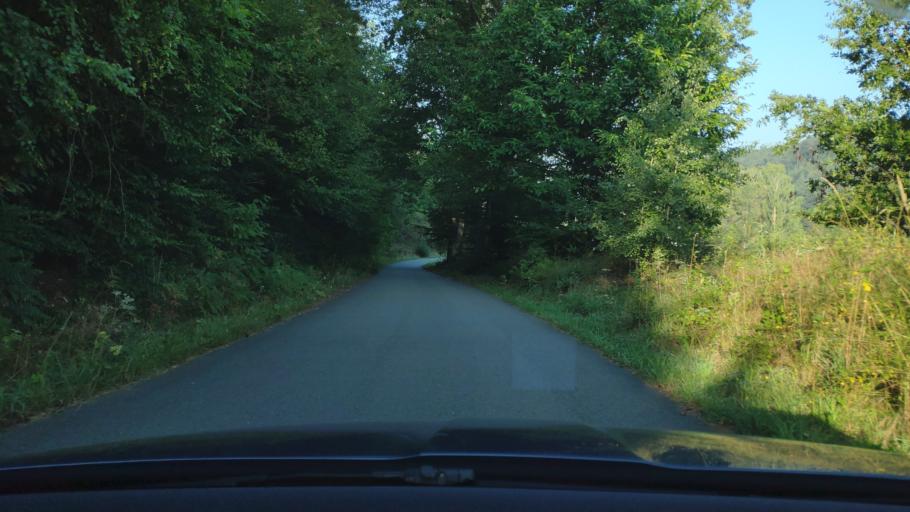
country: DE
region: Rheinland-Pfalz
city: Fischbach
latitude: 49.0658
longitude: 7.7047
